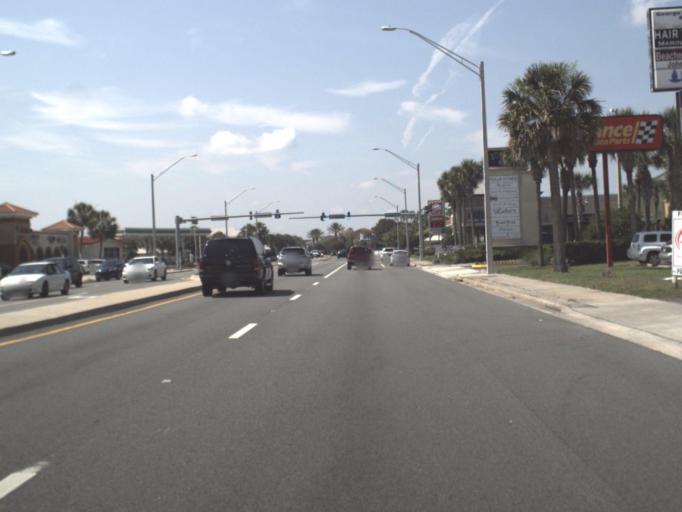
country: US
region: Florida
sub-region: Duval County
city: Jacksonville Beach
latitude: 30.2687
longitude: -81.3886
